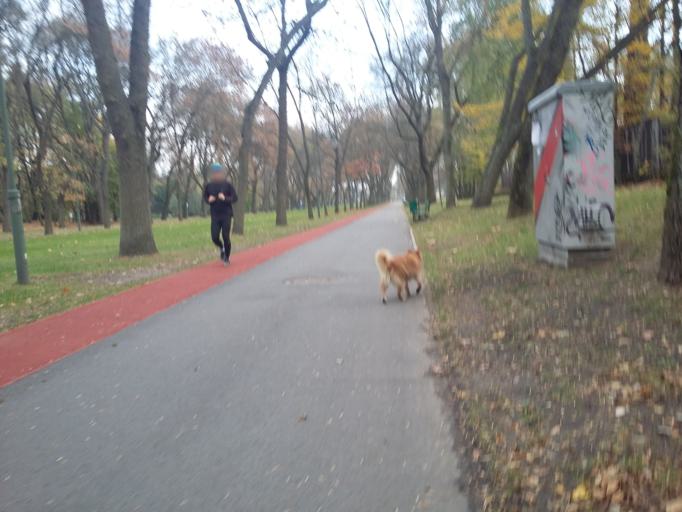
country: PL
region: Lodz Voivodeship
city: Lodz
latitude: 51.7642
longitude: 19.4193
